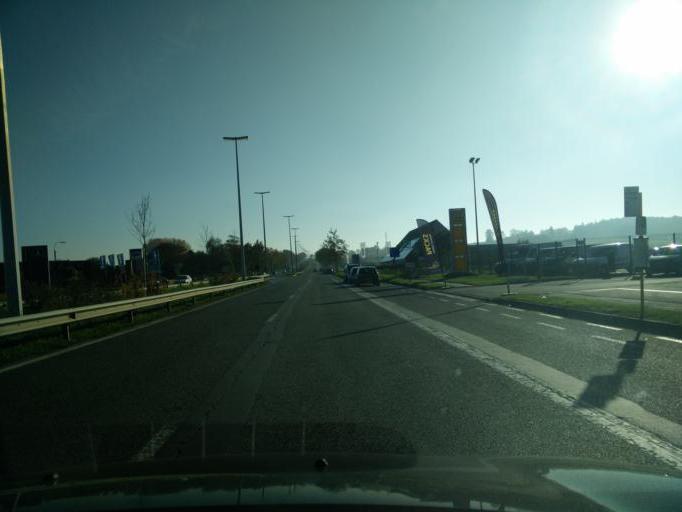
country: BE
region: Flanders
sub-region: Provincie Oost-Vlaanderen
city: Oudenaarde
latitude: 50.8246
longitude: 3.6037
